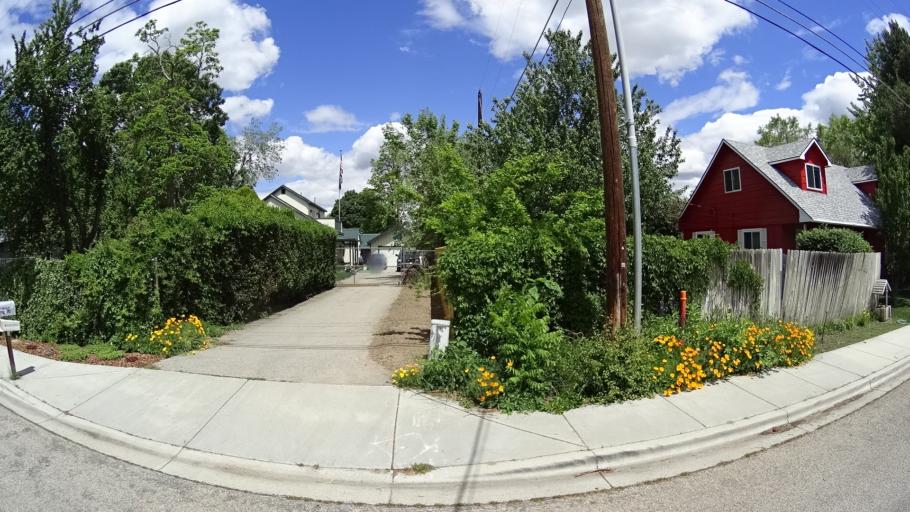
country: US
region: Idaho
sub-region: Ada County
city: Boise
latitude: 43.5844
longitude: -116.1890
